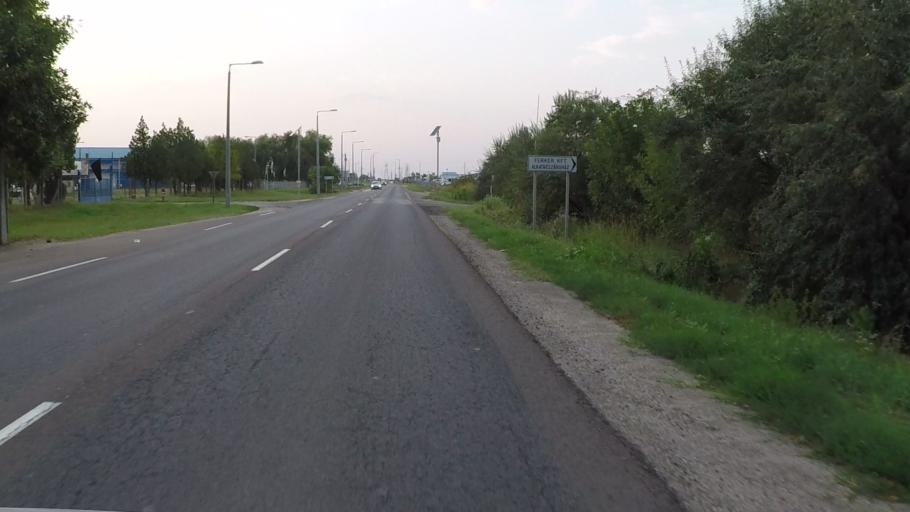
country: HU
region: Jasz-Nagykun-Szolnok
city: Szolnok
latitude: 47.1987
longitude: 20.1630
